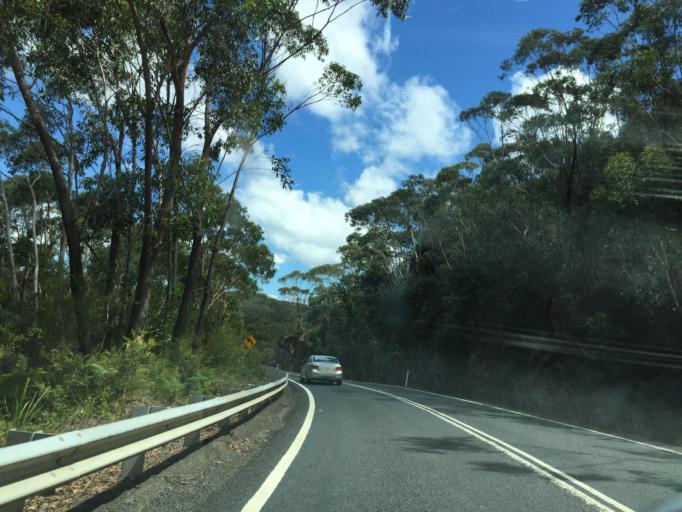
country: AU
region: New South Wales
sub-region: Blue Mountains Municipality
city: Blackheath
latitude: -33.5550
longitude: 150.3763
